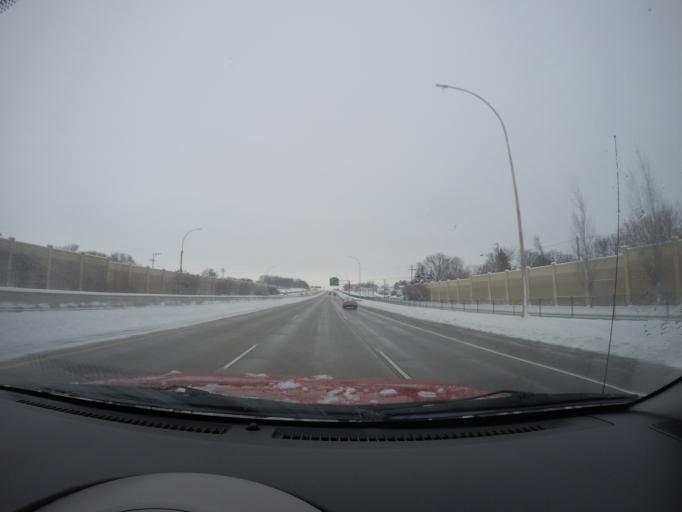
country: US
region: Minnesota
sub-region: Olmsted County
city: Rochester
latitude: 44.0514
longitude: -92.4925
